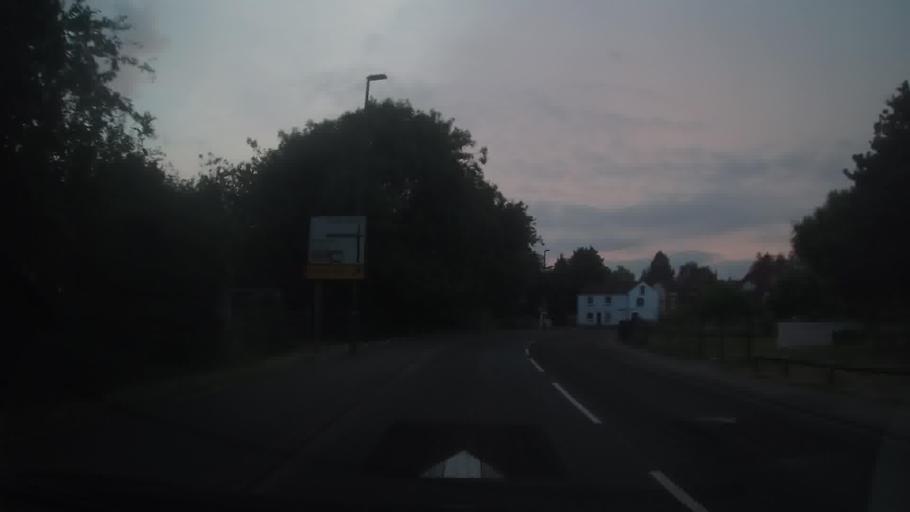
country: GB
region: England
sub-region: Leicestershire
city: Mountsorrel
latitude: 52.7071
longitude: -1.1360
